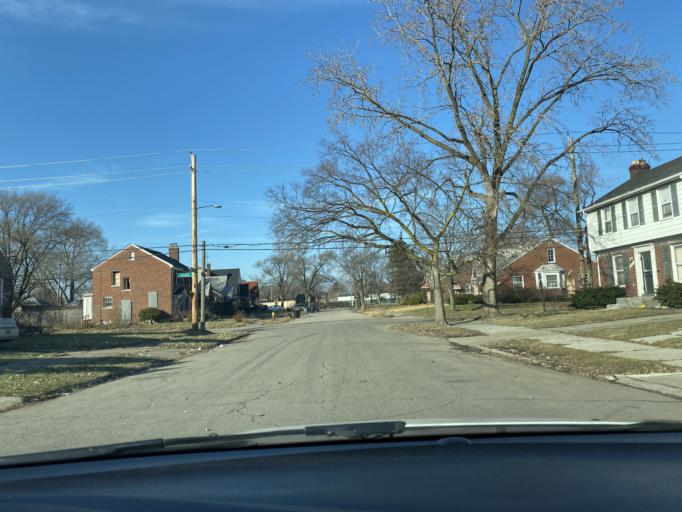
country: US
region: Michigan
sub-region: Wayne County
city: Grosse Pointe Park
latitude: 42.4065
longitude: -82.9498
